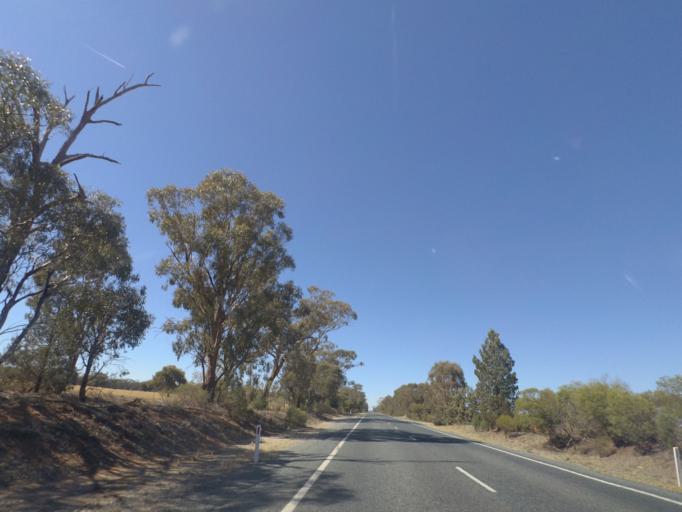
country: AU
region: New South Wales
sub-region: Bland
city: West Wyalong
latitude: -34.1578
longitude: 147.1173
